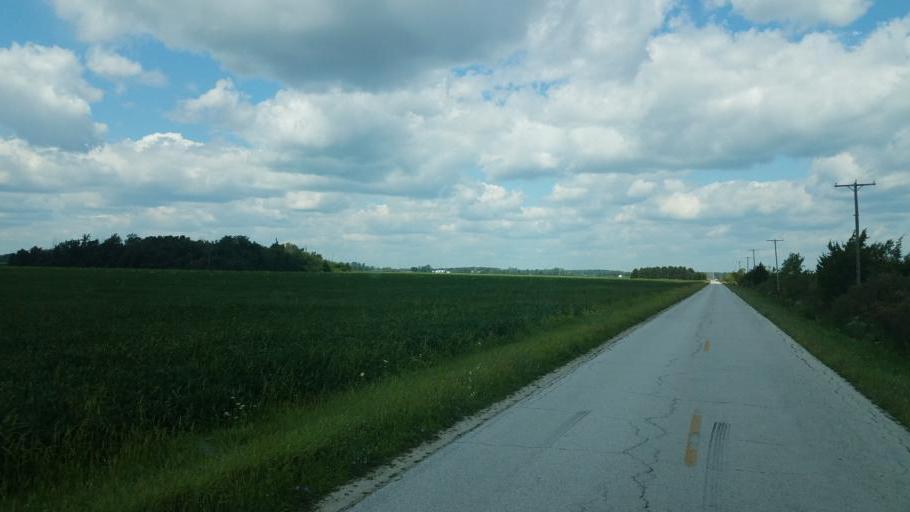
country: US
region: Ohio
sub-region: Sandusky County
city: Gibsonburg
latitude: 41.3888
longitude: -83.3390
